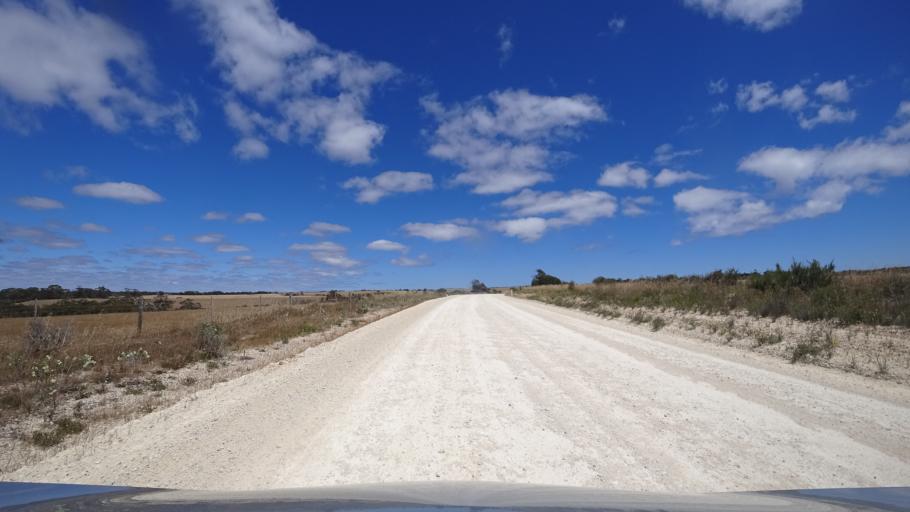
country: AU
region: South Australia
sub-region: Kangaroo Island
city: Kingscote
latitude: -35.6482
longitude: 137.3643
